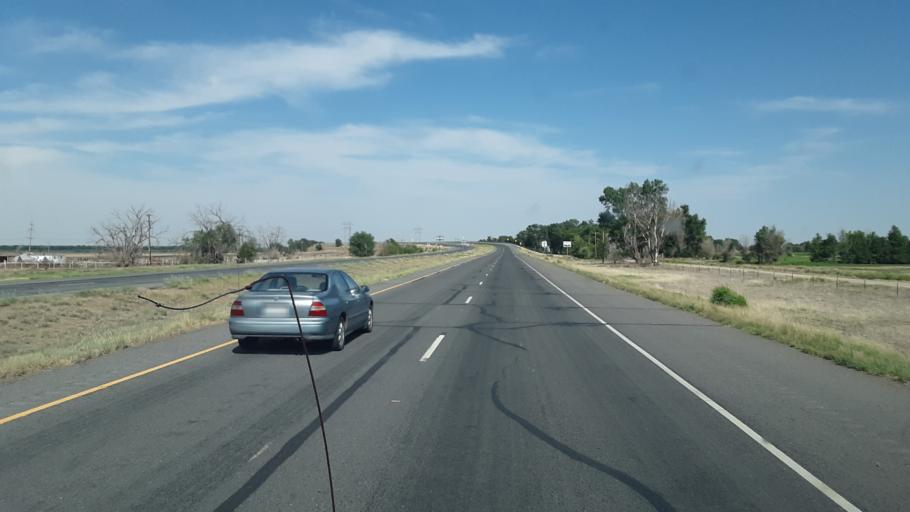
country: US
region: Colorado
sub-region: Otero County
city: Rocky Ford
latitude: 38.1030
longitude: -103.8511
